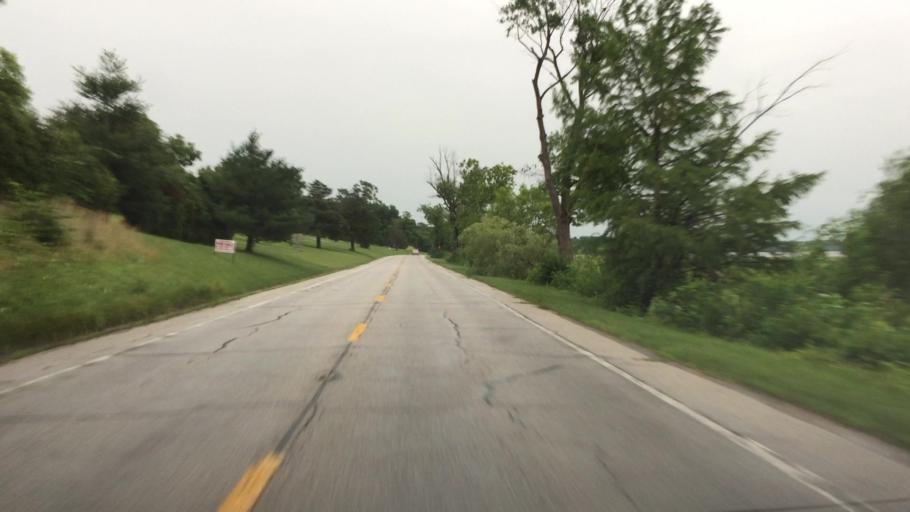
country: US
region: Illinois
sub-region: Hancock County
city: Nauvoo
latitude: 40.5295
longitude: -91.3720
